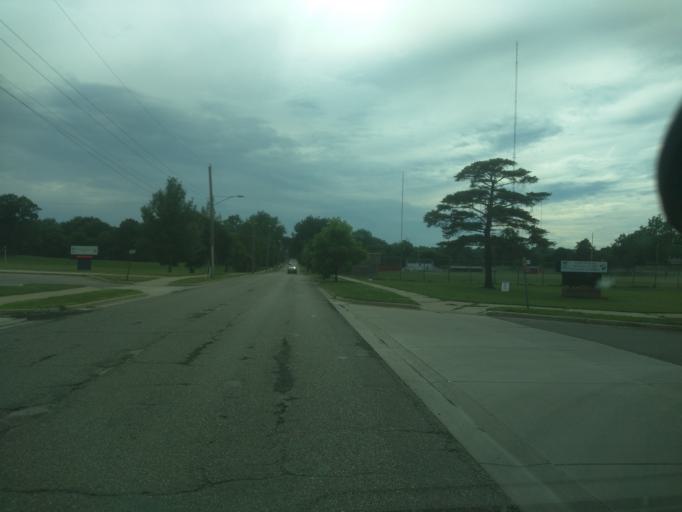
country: US
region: Michigan
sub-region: Ingham County
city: Lansing
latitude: 42.6902
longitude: -84.5543
